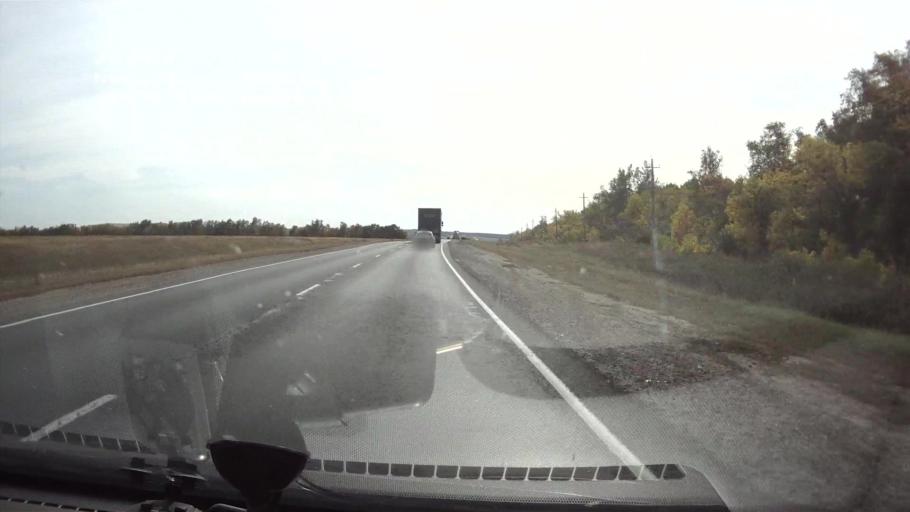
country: RU
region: Saratov
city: Alekseyevka
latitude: 52.2706
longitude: 47.9290
